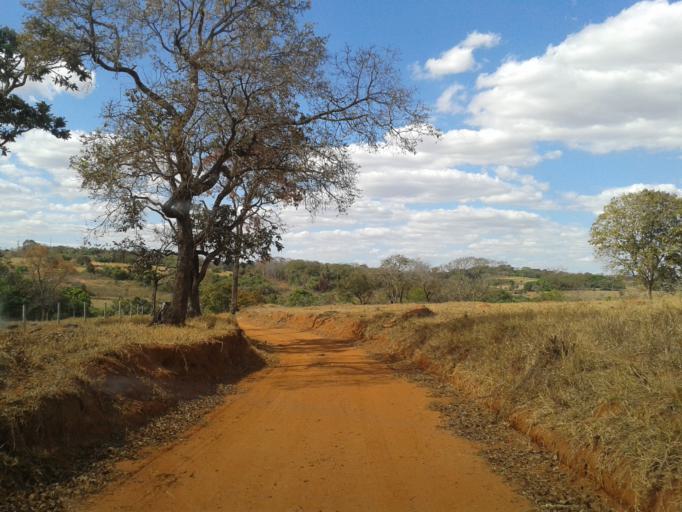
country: BR
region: Minas Gerais
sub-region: Monte Alegre De Minas
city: Monte Alegre de Minas
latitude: -18.7941
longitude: -49.0862
